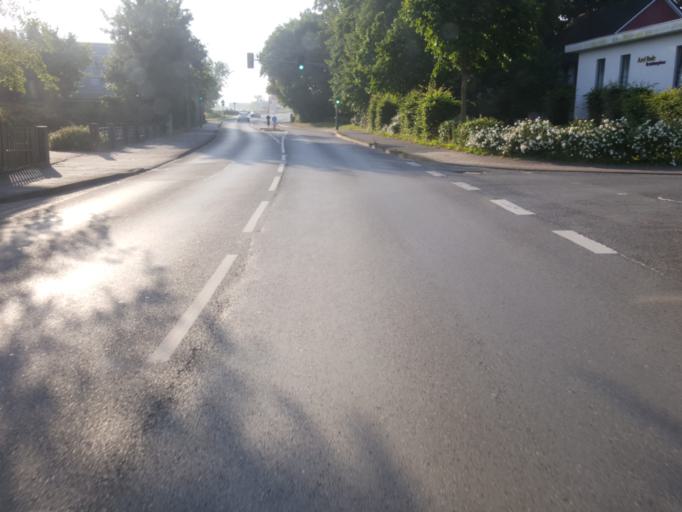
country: DE
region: North Rhine-Westphalia
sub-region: Regierungsbezirk Detmold
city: Kirchlengern
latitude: 52.1927
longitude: 8.6288
